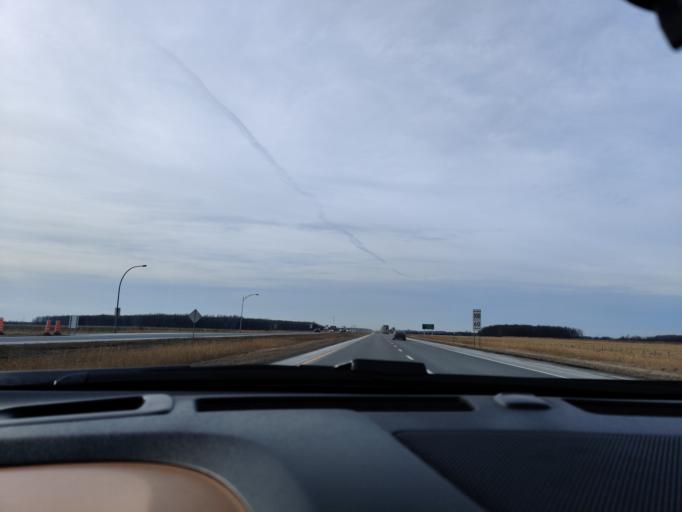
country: CA
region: Quebec
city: Les Cedres
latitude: 45.3395
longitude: -74.0905
